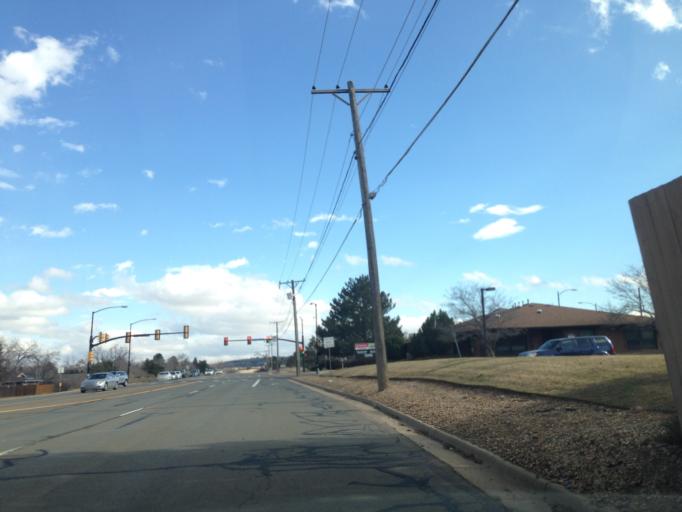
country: US
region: Colorado
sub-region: Boulder County
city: Boulder
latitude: 39.9763
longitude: -105.2417
